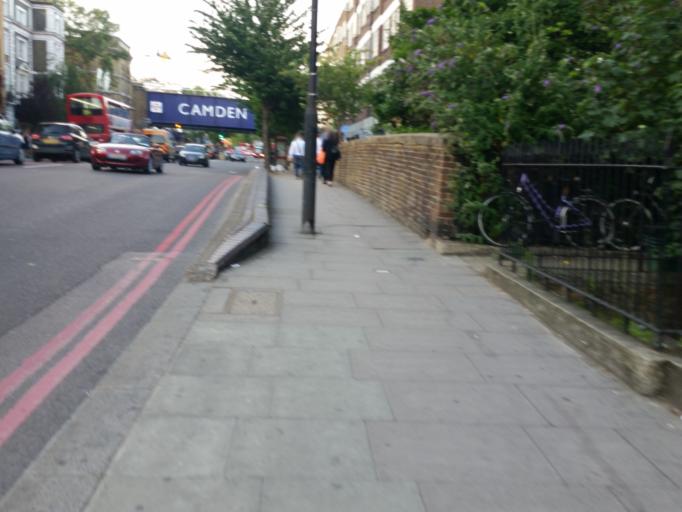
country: GB
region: England
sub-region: Greater London
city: Camden Town
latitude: 51.5409
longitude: -0.1392
